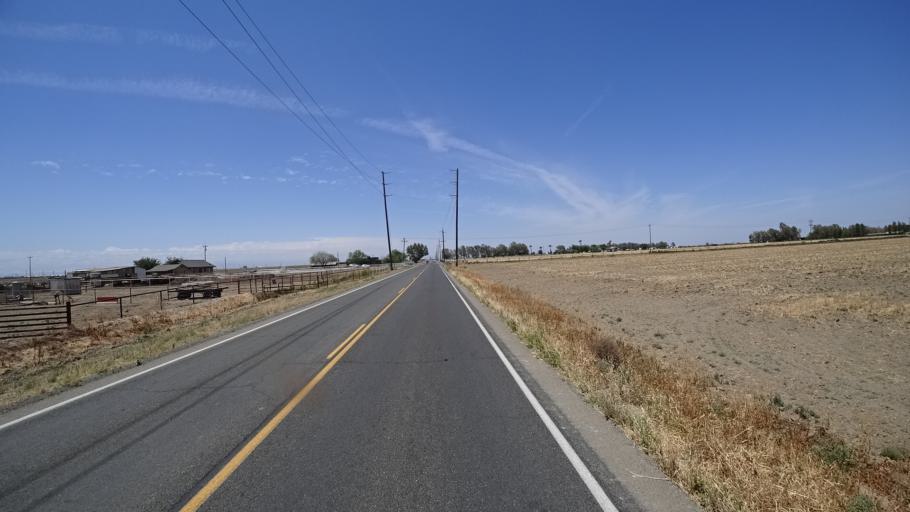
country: US
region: California
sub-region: Kings County
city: Stratford
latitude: 36.2403
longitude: -119.7967
